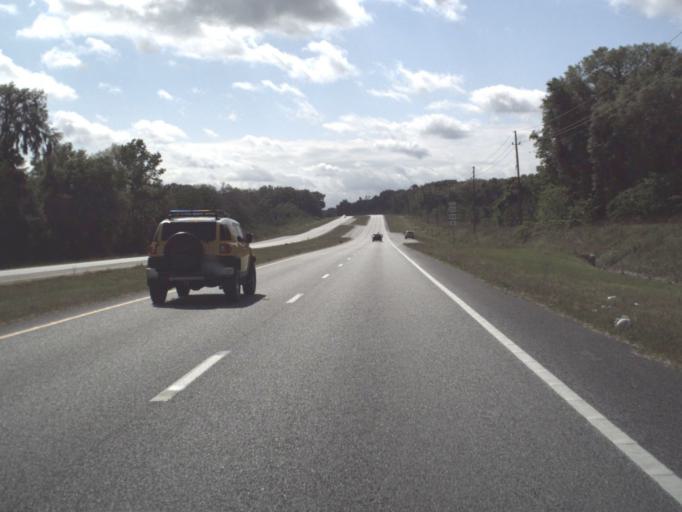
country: US
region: Florida
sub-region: Marion County
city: Ocala
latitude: 29.2652
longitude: -82.1736
